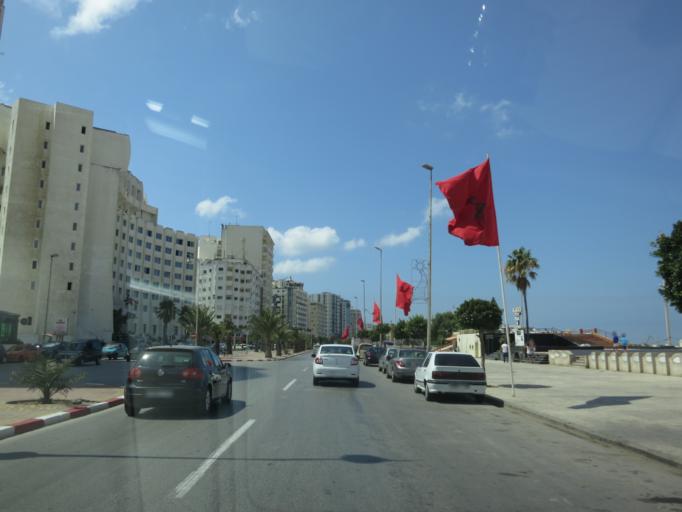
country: MA
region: Tanger-Tetouan
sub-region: Tanger-Assilah
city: Tangier
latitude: 35.7768
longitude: -5.7965
